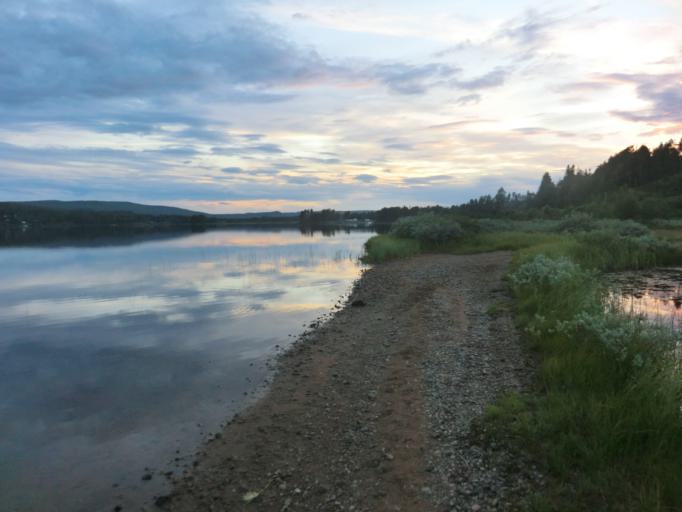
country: NO
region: Hedmark
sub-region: Trysil
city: Innbygda
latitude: 61.8527
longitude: 12.7464
